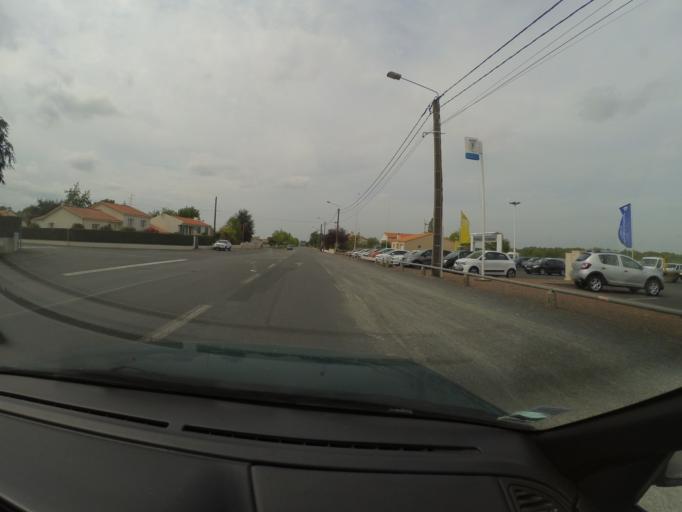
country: FR
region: Pays de la Loire
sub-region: Departement de la Loire-Atlantique
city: Gorges
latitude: 47.0968
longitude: -1.2945
